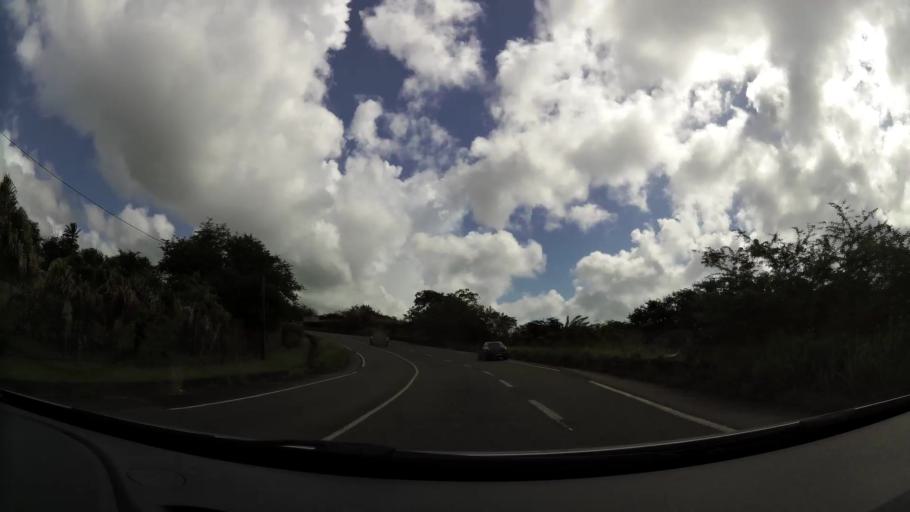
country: MQ
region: Martinique
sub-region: Martinique
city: Les Trois-Ilets
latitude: 14.4821
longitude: -60.9995
